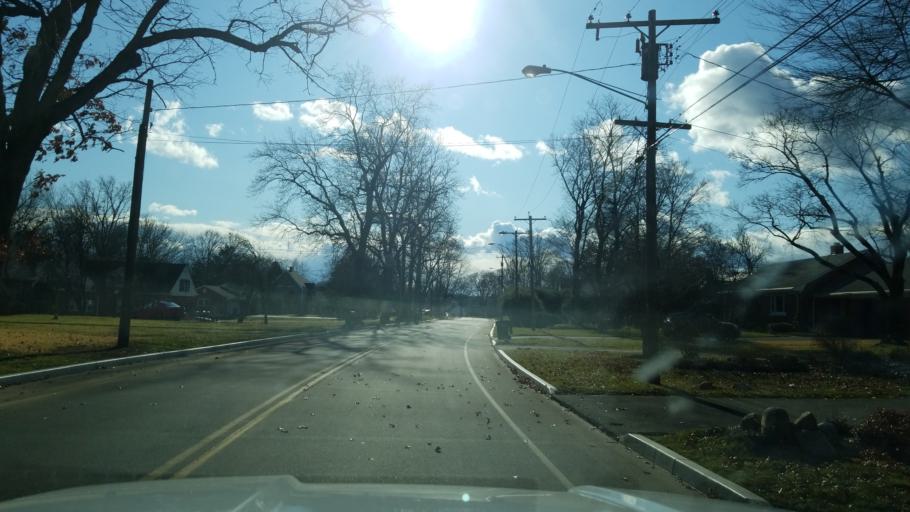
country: US
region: Connecticut
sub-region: Middlesex County
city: Middletown
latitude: 41.5597
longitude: -72.6742
